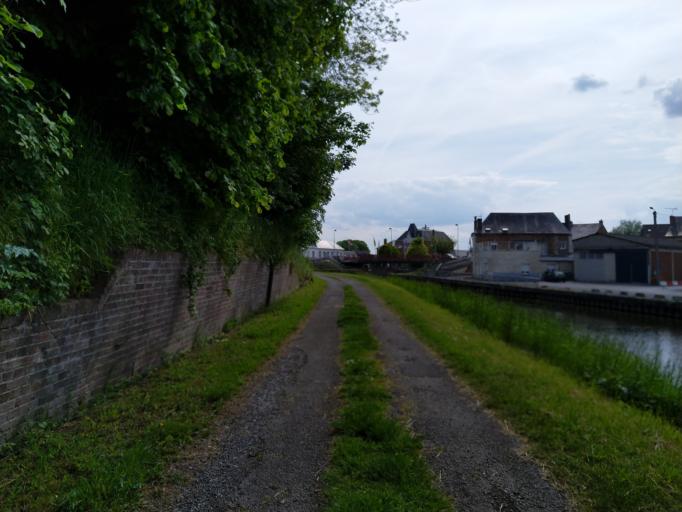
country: FR
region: Picardie
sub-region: Departement de l'Aisne
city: Etreux
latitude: 49.9919
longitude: 3.6561
